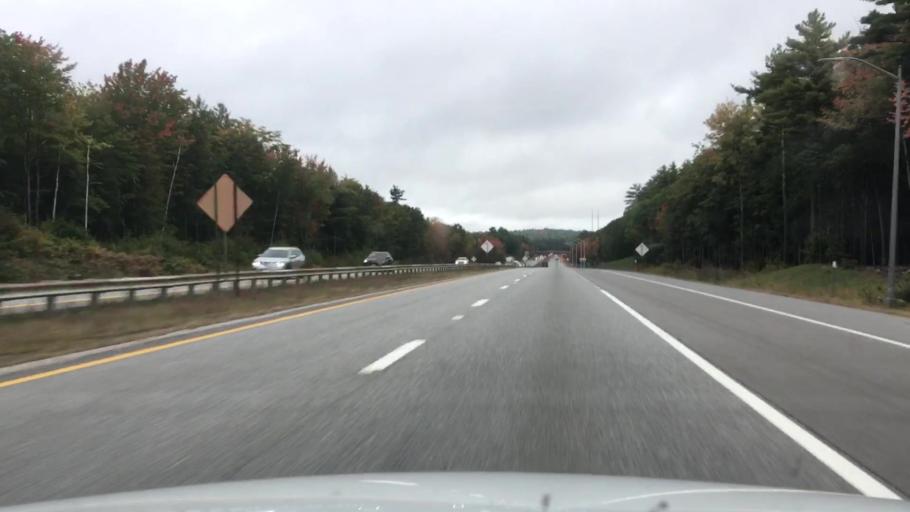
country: US
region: Maine
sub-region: Cumberland County
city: Cumberland Center
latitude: 43.8266
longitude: -70.3214
